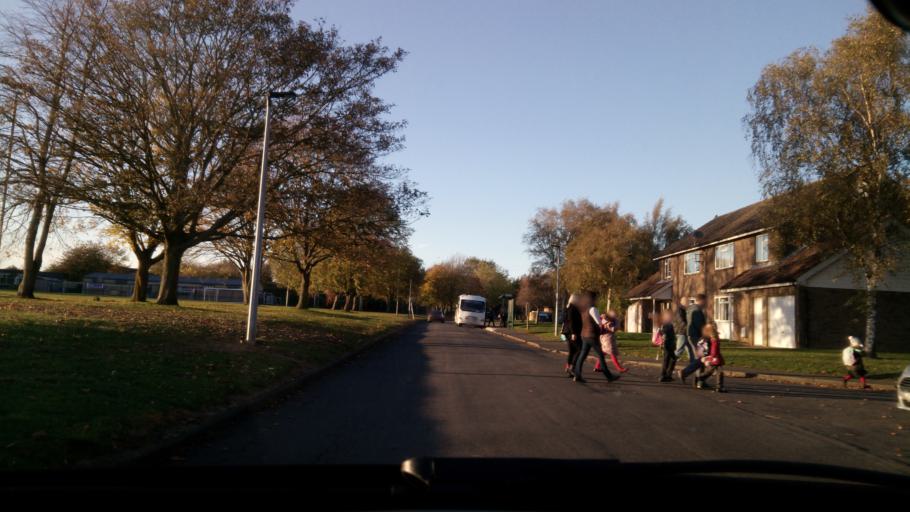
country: GB
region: England
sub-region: Peterborough
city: Wittering
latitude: 52.6095
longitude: -0.4406
